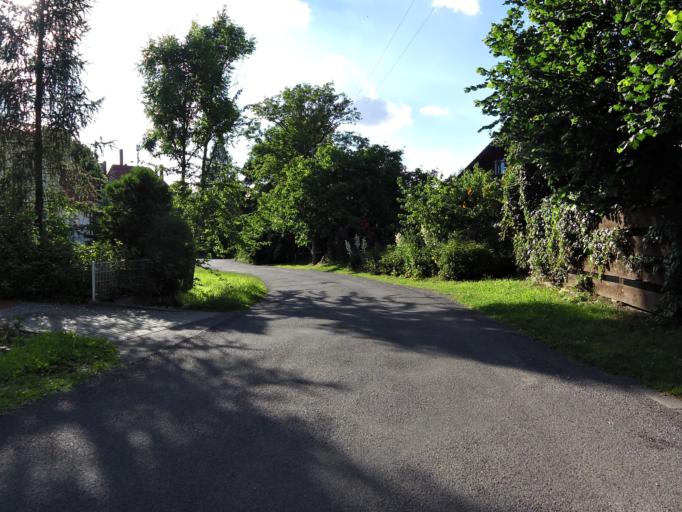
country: DE
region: Saxony
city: Taucha
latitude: 51.3241
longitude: 12.4553
